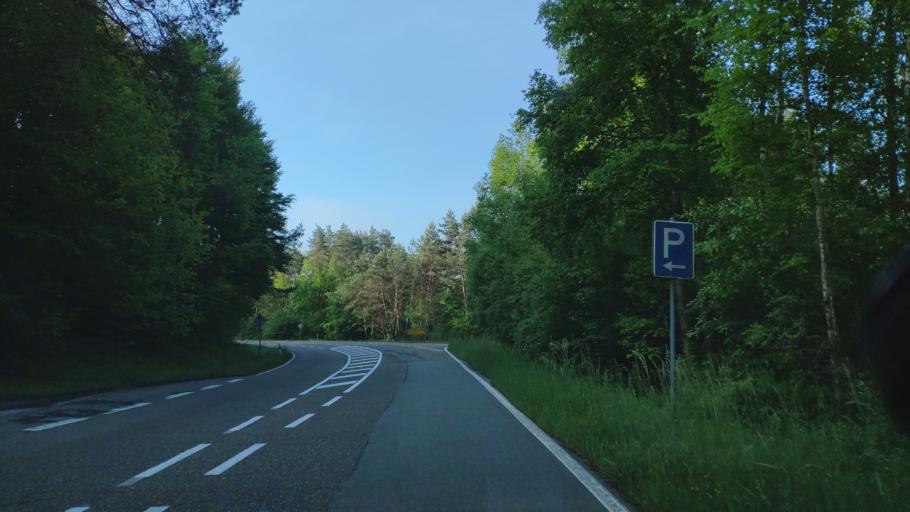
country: DE
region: Rheinland-Pfalz
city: Ludwigswinkel
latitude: 49.0876
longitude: 7.6815
